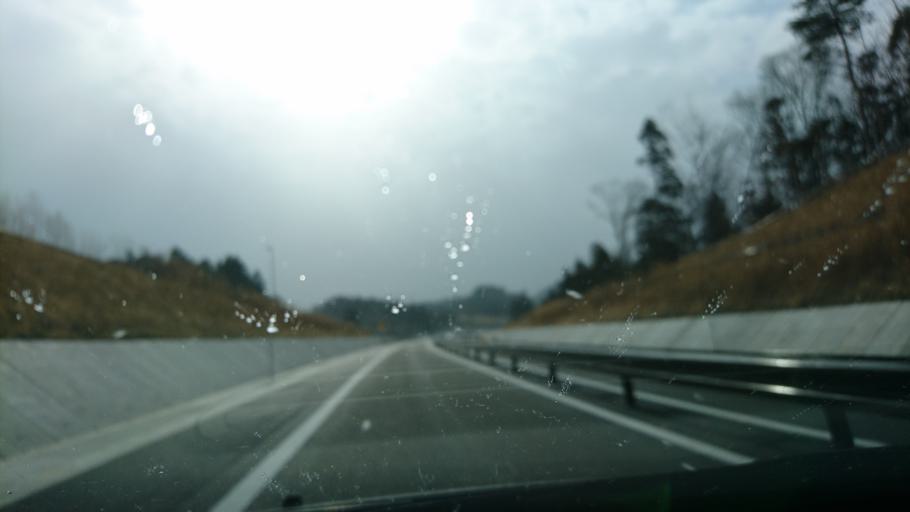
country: JP
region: Iwate
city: Ofunato
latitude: 38.8029
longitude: 141.5380
